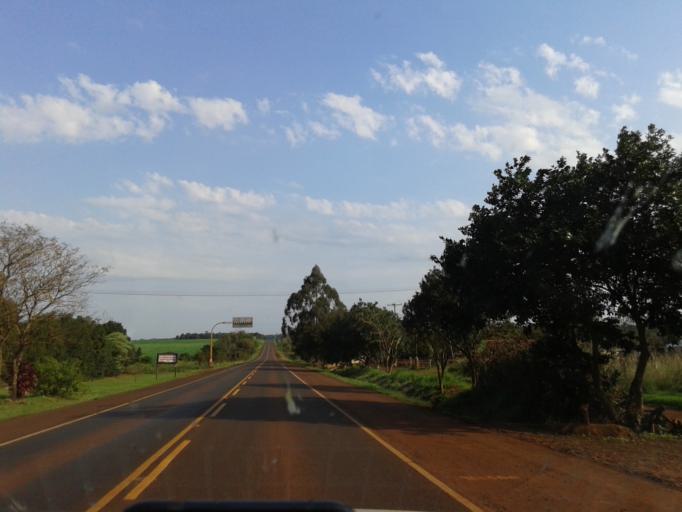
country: PY
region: Itapua
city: Edelira
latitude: -26.7650
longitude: -55.3863
